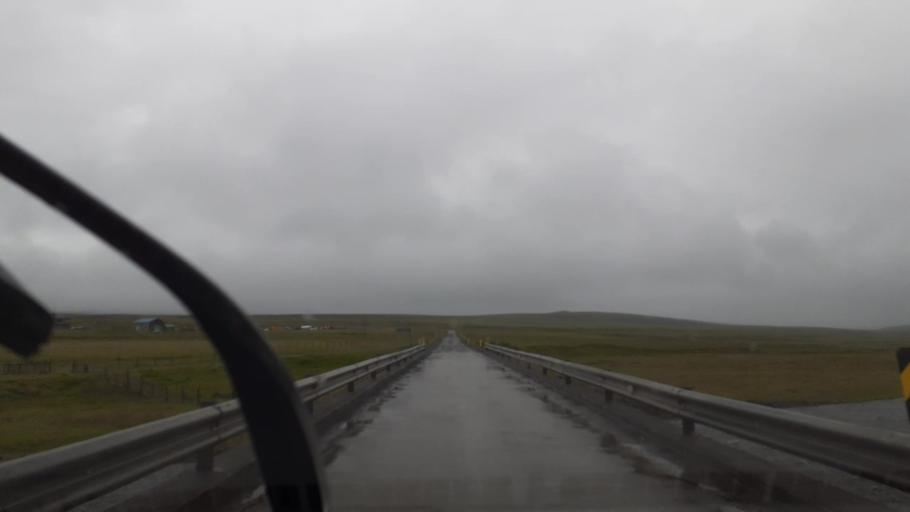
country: IS
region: East
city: Egilsstadir
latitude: 66.0408
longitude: -15.1002
